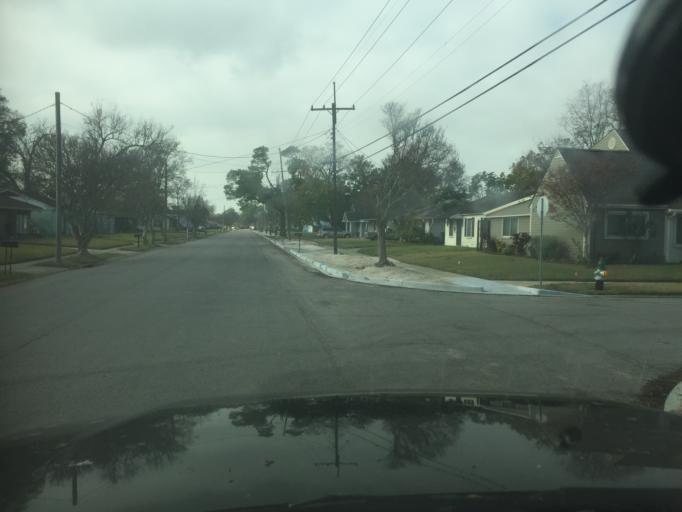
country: US
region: Louisiana
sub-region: Saint Bernard Parish
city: Arabi
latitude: 30.0068
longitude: -90.0378
